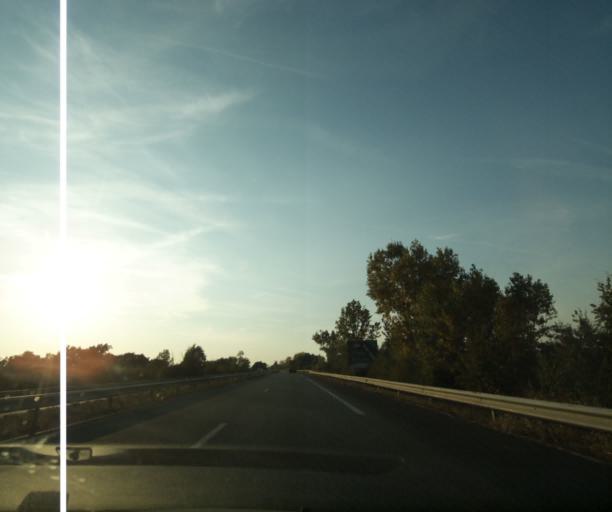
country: FR
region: Midi-Pyrenees
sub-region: Departement du Tarn-et-Garonne
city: Saint-Nicolas-de-la-Grave
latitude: 44.0481
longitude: 0.9861
